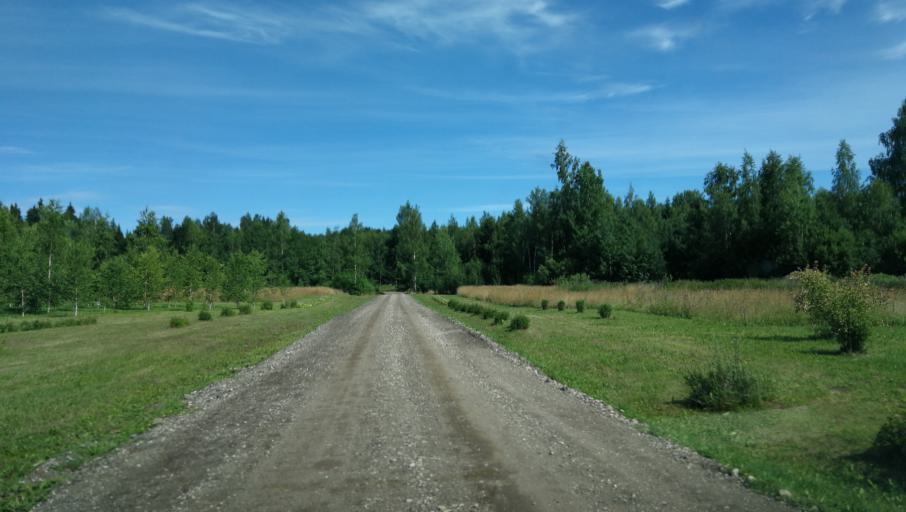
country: LV
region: Gulbenes Rajons
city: Gulbene
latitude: 57.1668
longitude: 26.8723
